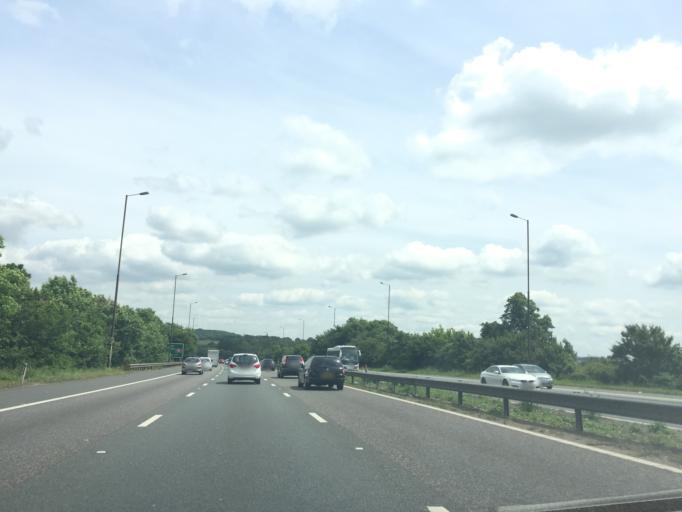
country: GB
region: England
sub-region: Kent
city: Dartford
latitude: 51.4262
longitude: 0.2233
